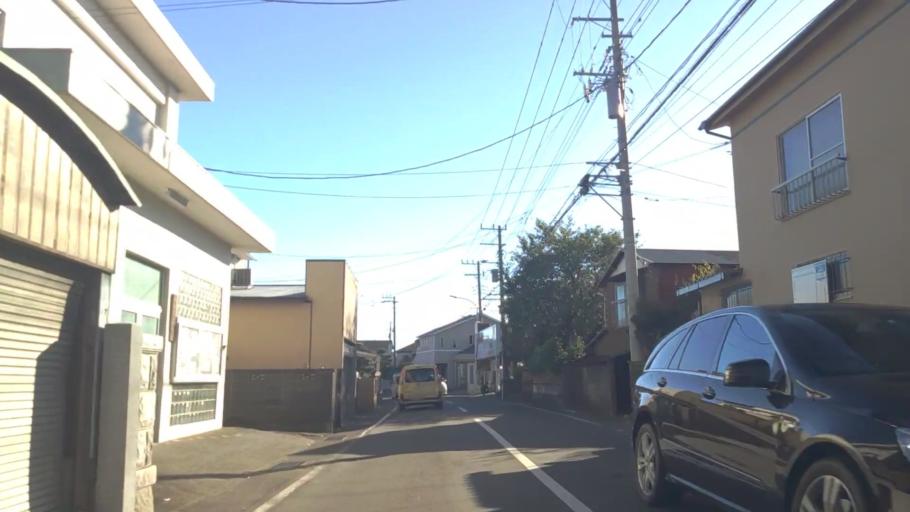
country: JP
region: Kanagawa
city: Atsugi
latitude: 35.3864
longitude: 139.3665
